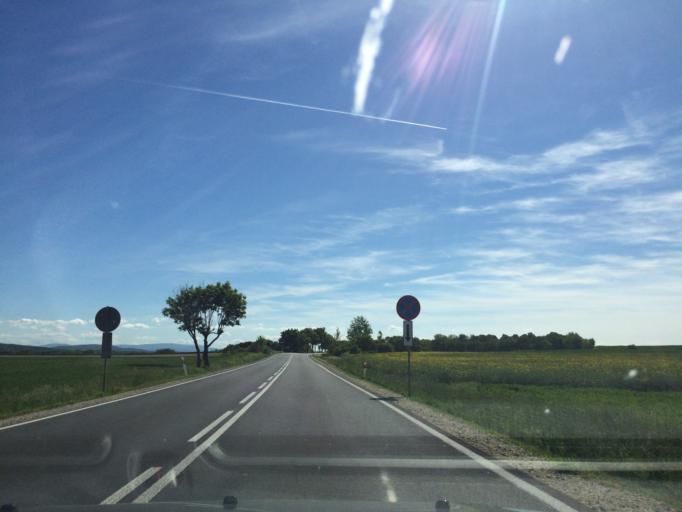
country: PL
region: Lower Silesian Voivodeship
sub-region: Powiat wroclawski
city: Sobotka
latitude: 50.9360
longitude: 16.7092
